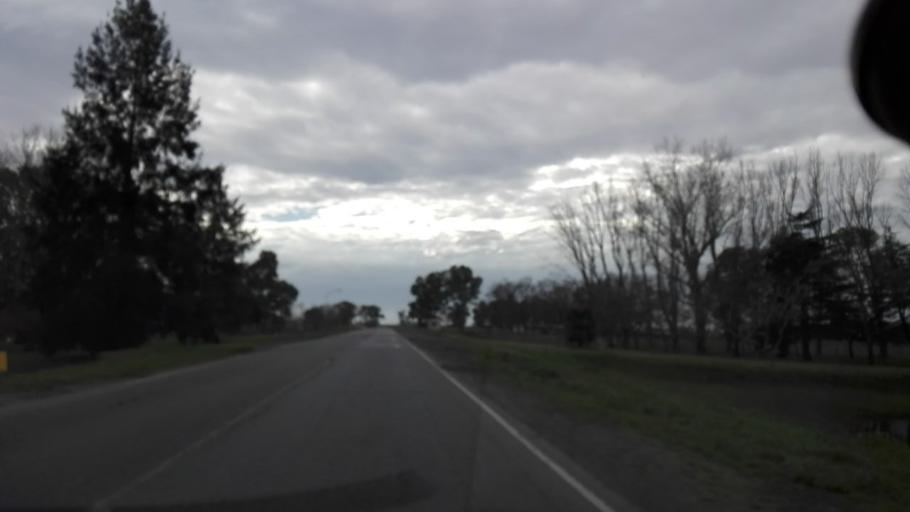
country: AR
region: Buenos Aires
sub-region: Partido de Las Flores
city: Las Flores
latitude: -36.2180
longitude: -59.0447
